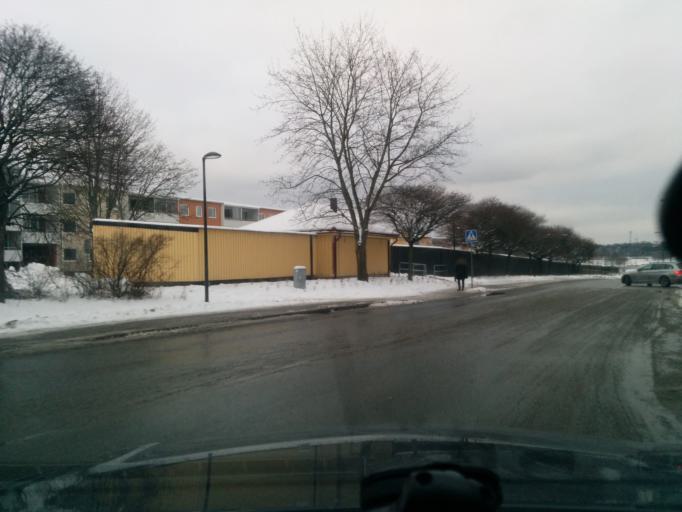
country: SE
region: Stockholm
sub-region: Taby Kommun
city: Taby
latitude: 59.4468
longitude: 18.0731
